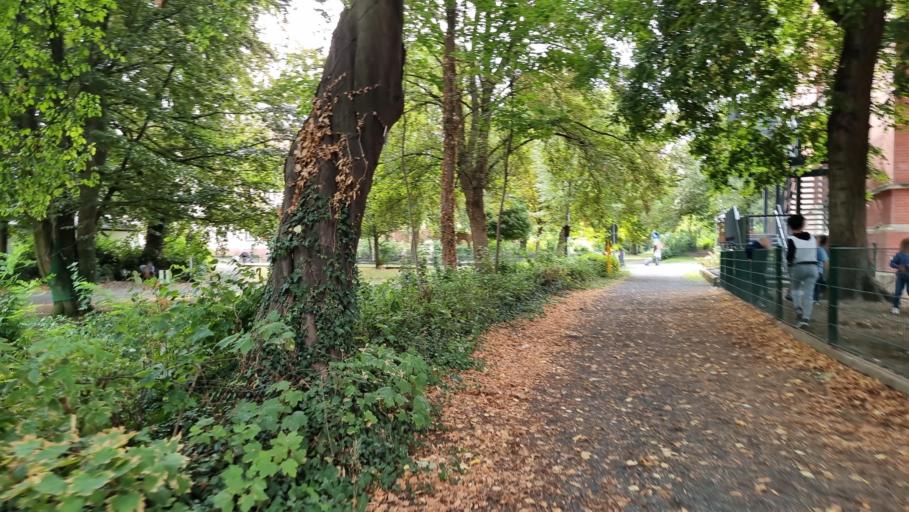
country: DE
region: Lower Saxony
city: Alfeld
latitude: 51.9878
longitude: 9.8276
